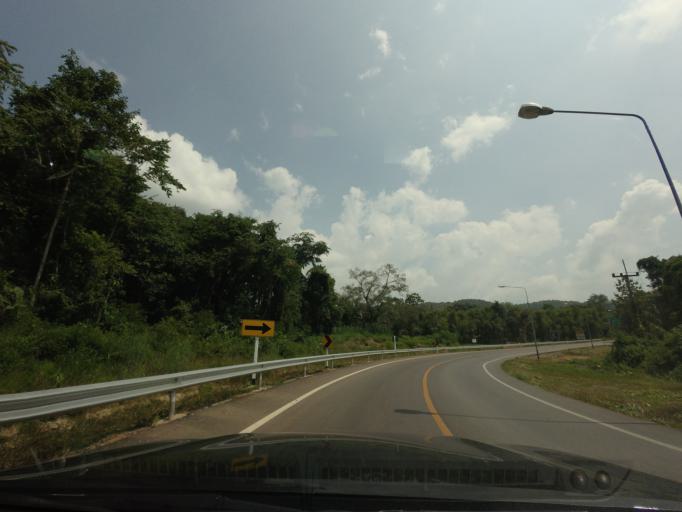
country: TH
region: Nan
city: Santi Suk
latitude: 18.9869
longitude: 100.9360
